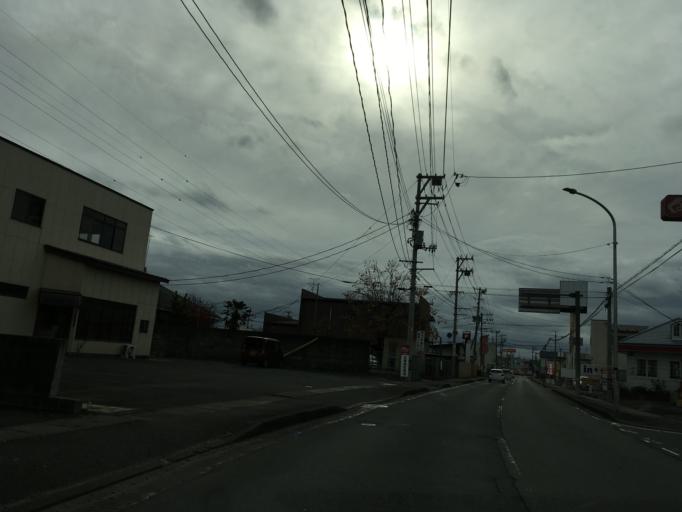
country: JP
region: Miyagi
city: Wakuya
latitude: 38.6910
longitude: 141.2062
